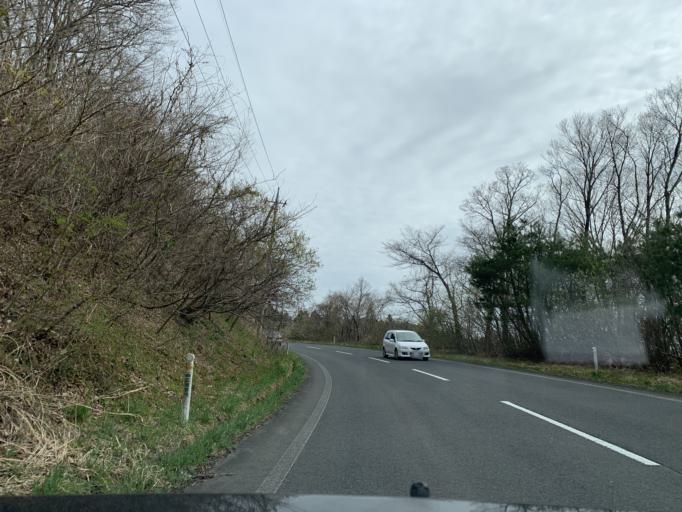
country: JP
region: Iwate
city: Ichinoseki
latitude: 38.8233
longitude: 141.3031
